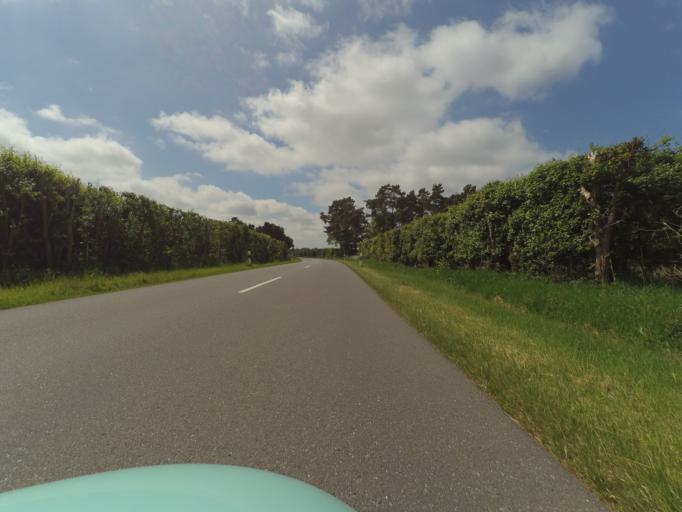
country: DE
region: Lower Saxony
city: Hillerse
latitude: 52.4283
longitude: 10.3637
